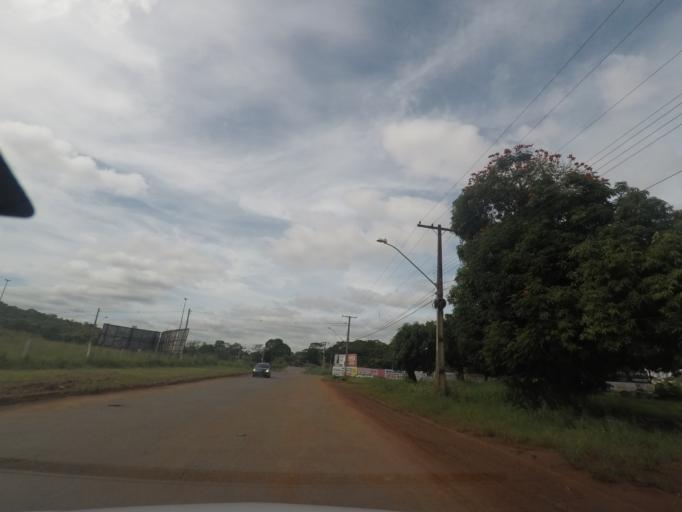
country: BR
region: Goias
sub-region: Goiania
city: Goiania
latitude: -16.6738
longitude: -49.2001
